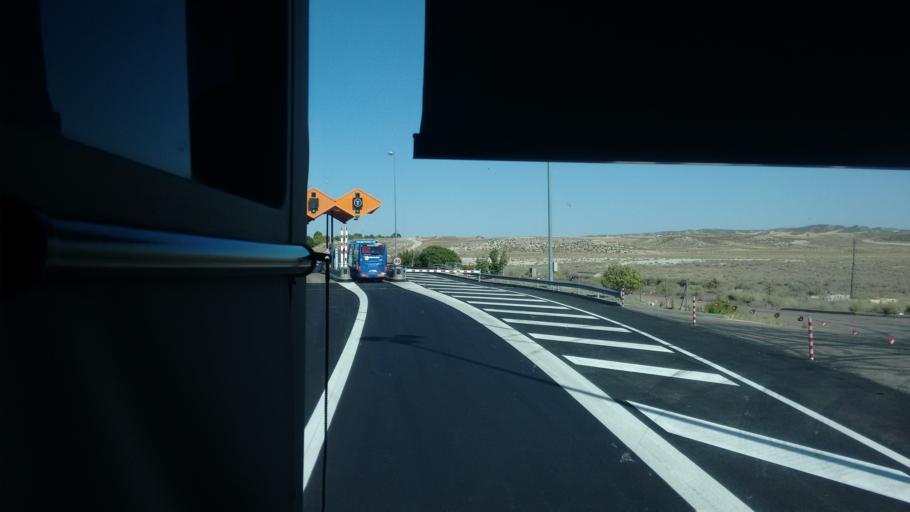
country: ES
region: Aragon
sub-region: Provincia de Zaragoza
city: Pina de Ebro
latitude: 41.5178
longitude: -0.4359
